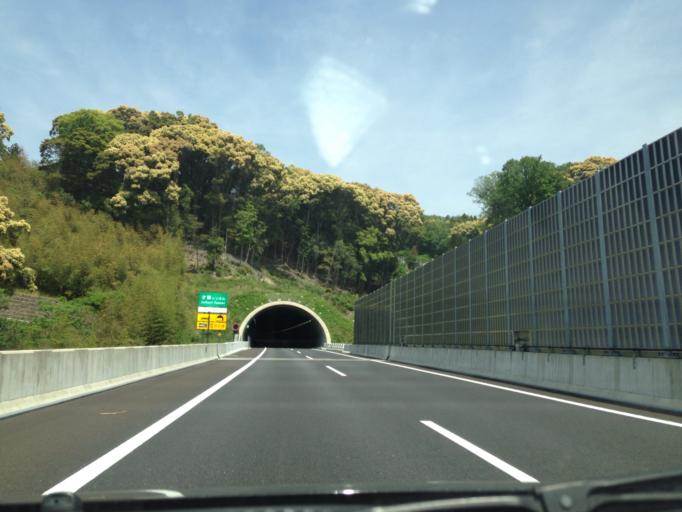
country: JP
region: Aichi
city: Okazaki
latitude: 34.9590
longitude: 137.2537
